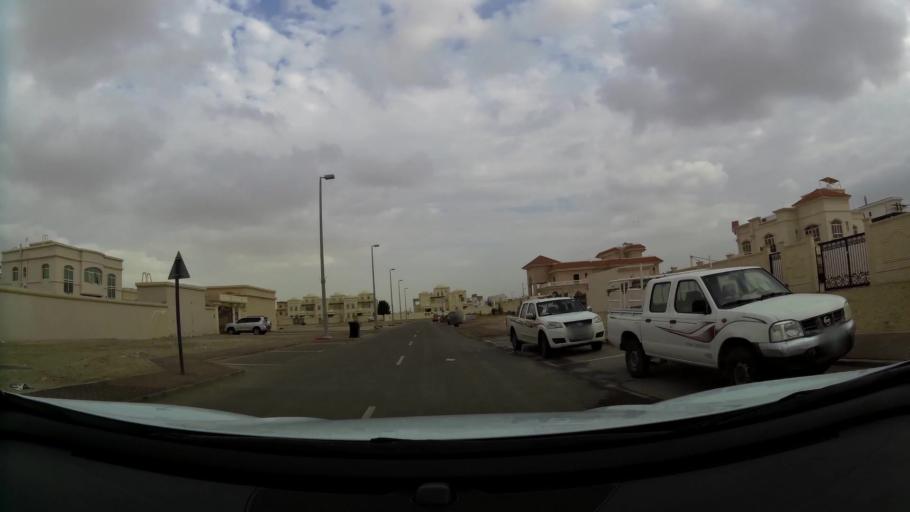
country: AE
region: Abu Dhabi
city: Abu Dhabi
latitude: 24.3458
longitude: 54.6170
